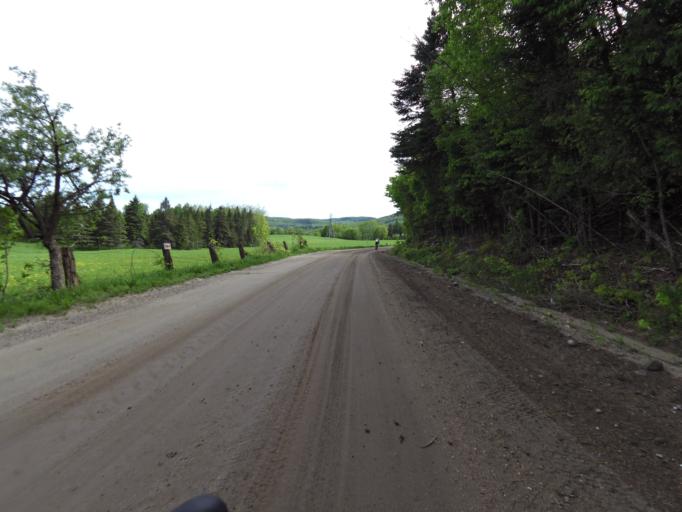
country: CA
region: Quebec
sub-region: Outaouais
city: Wakefield
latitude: 45.7159
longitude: -75.8933
